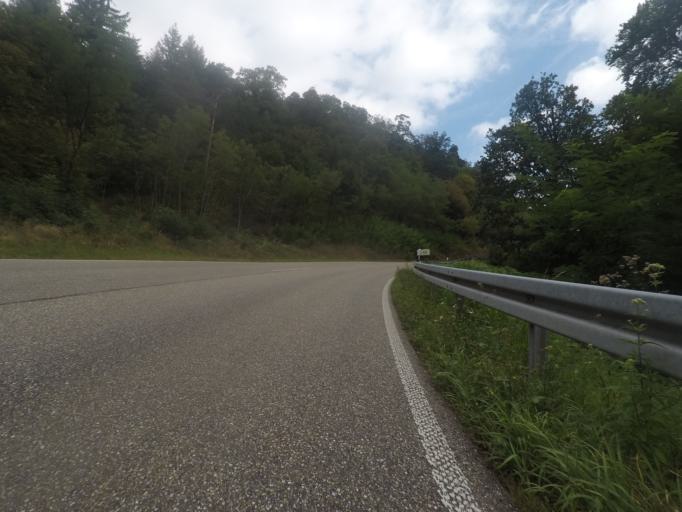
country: DE
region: Baden-Wuerttemberg
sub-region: Karlsruhe Region
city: Gaggenau
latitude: 48.8294
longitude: 8.3592
